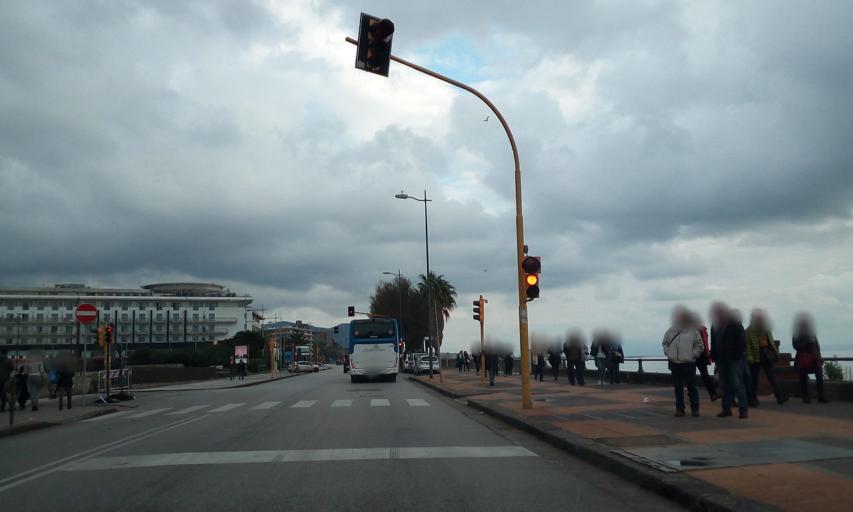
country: IT
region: Campania
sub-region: Provincia di Salerno
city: Salerno
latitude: 40.6729
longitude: 14.7729
